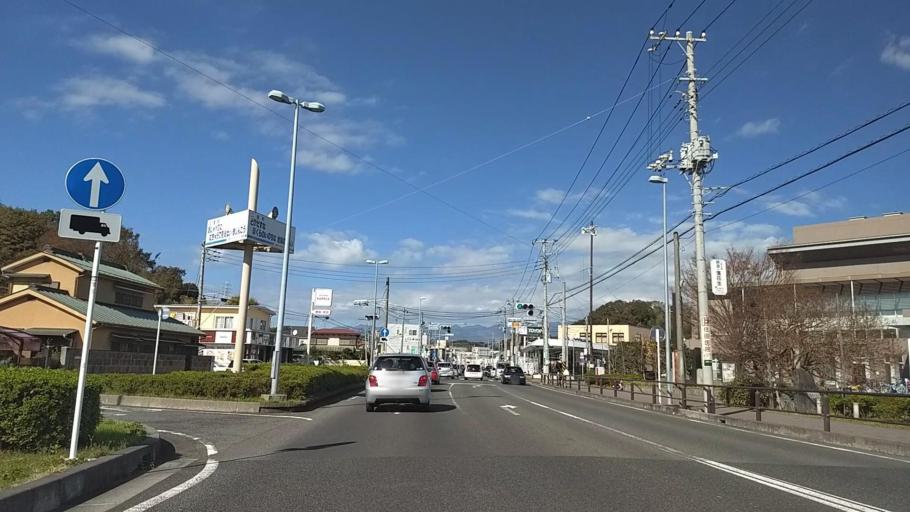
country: JP
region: Kanagawa
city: Ninomiya
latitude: 35.3030
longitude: 139.2577
